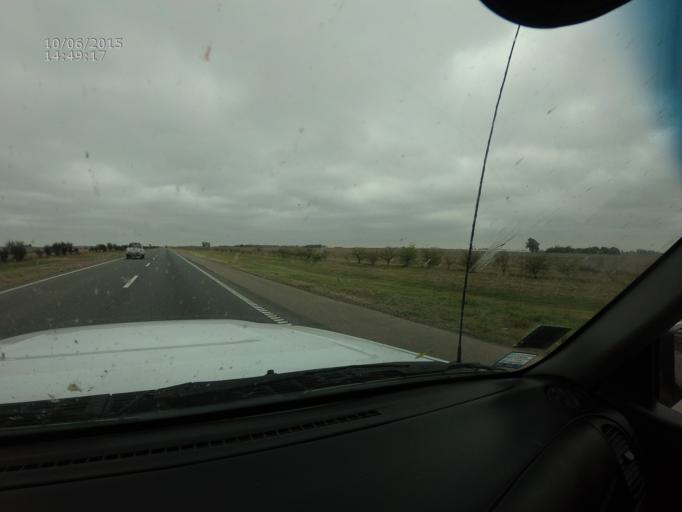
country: AR
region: Cordoba
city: Oncativo
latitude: -31.9306
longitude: -63.6160
